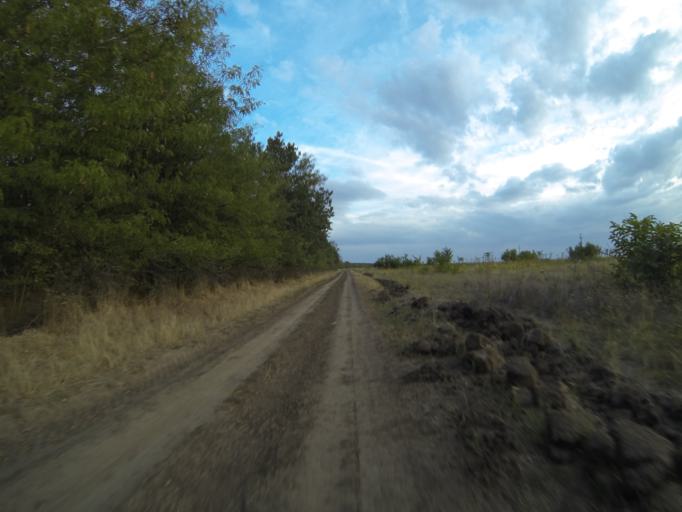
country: RO
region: Dolj
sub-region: Comuna Ceratu
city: Ceratu
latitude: 44.0916
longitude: 23.6731
